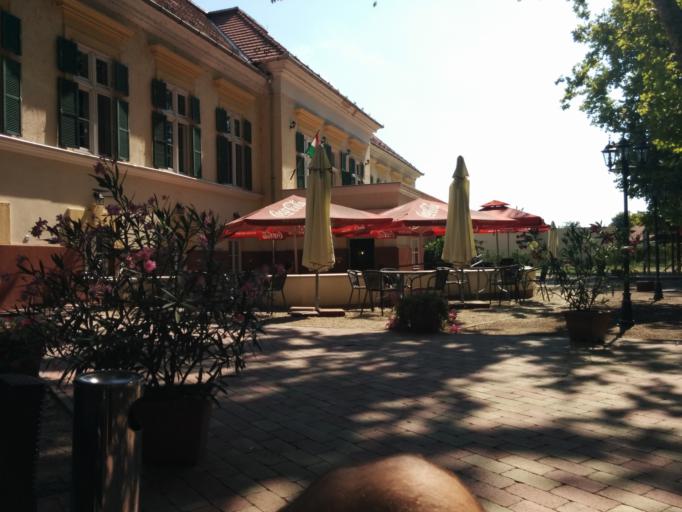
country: HU
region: Csongrad
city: Sandorfalva
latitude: 46.3605
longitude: 20.0984
